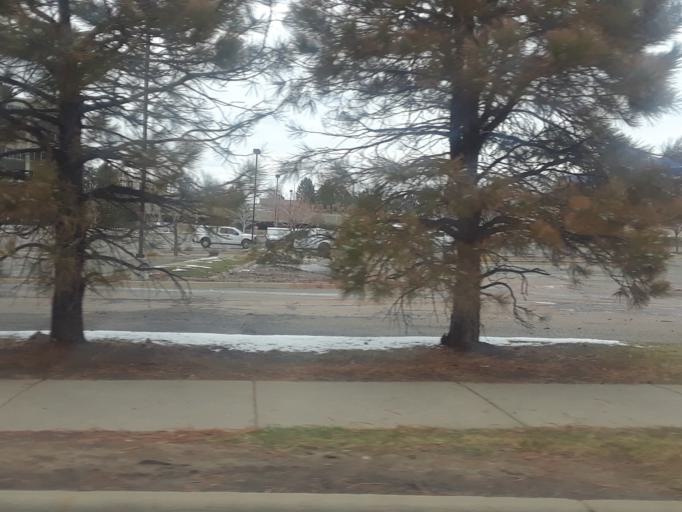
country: US
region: Colorado
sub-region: Arapahoe County
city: Centennial
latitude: 39.5697
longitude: -104.8771
